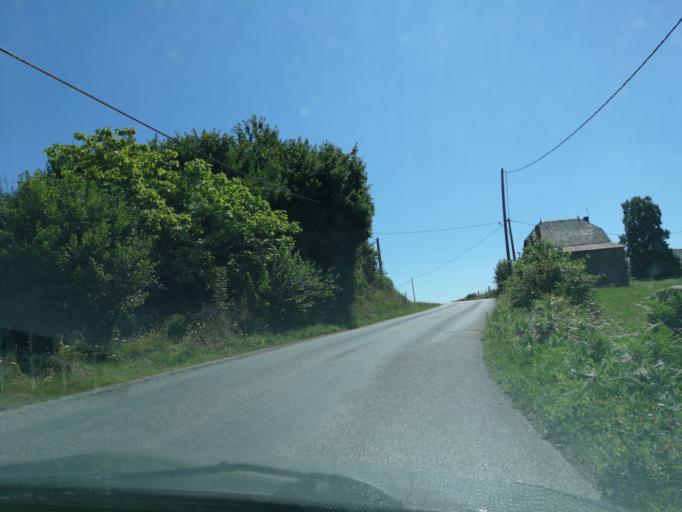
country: FR
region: Limousin
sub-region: Departement de la Correze
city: Argentat
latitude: 45.1038
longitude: 1.8826
